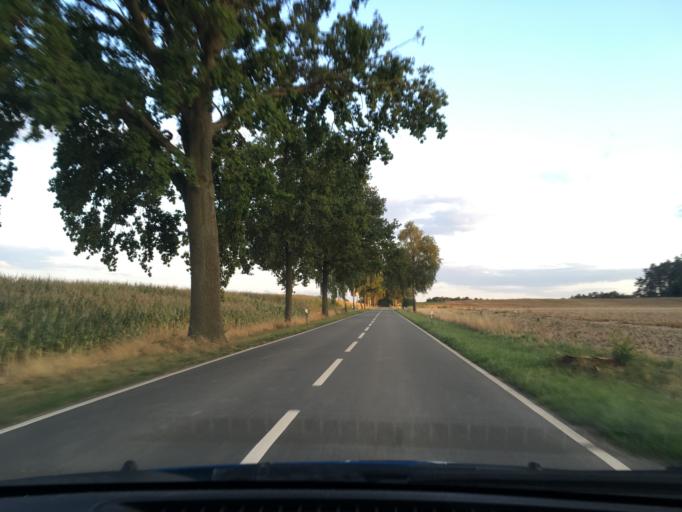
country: DE
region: Lower Saxony
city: Tosterglope
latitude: 53.2224
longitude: 10.8096
